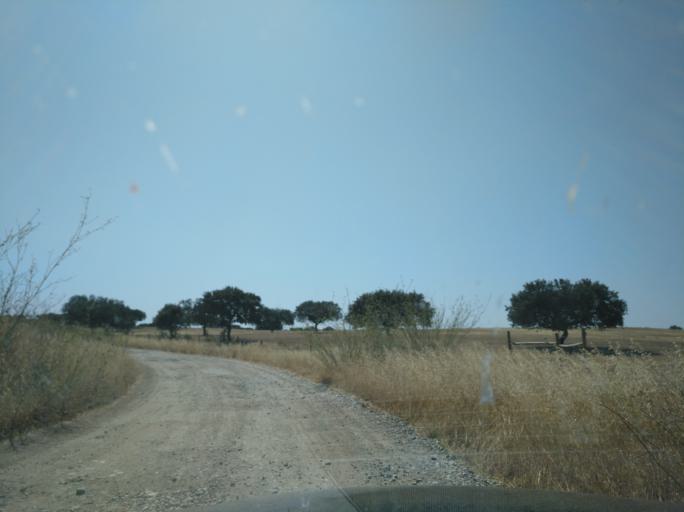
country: PT
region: Portalegre
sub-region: Campo Maior
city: Campo Maior
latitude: 39.0329
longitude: -6.9833
